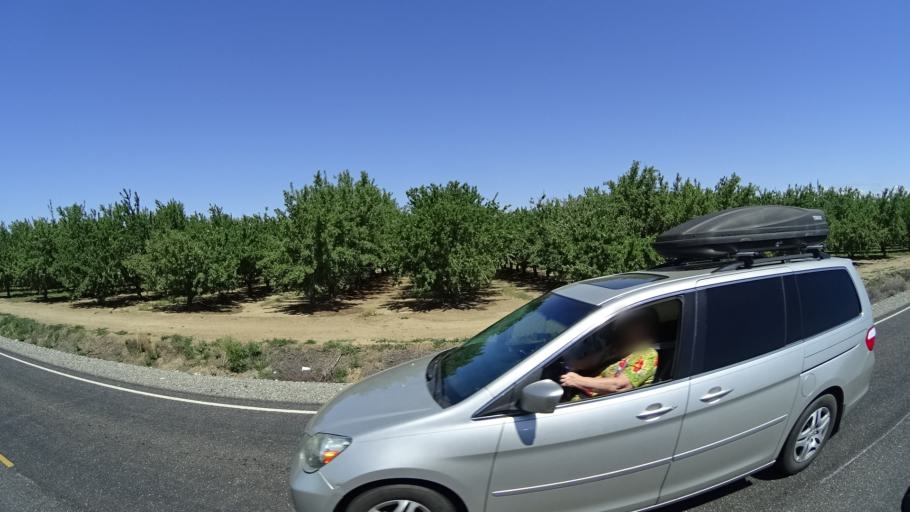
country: US
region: California
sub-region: Glenn County
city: Hamilton City
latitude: 39.7665
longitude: -122.0514
